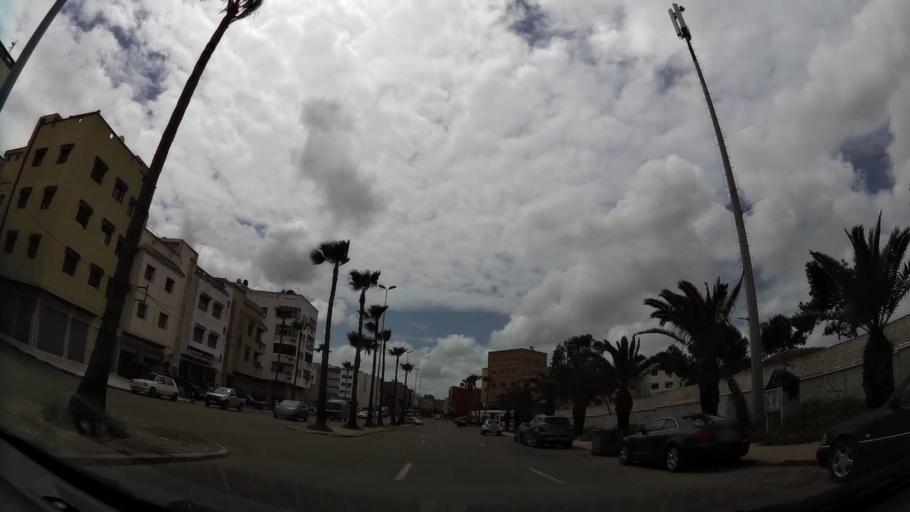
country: MA
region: Grand Casablanca
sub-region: Casablanca
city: Casablanca
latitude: 33.5388
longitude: -7.5946
